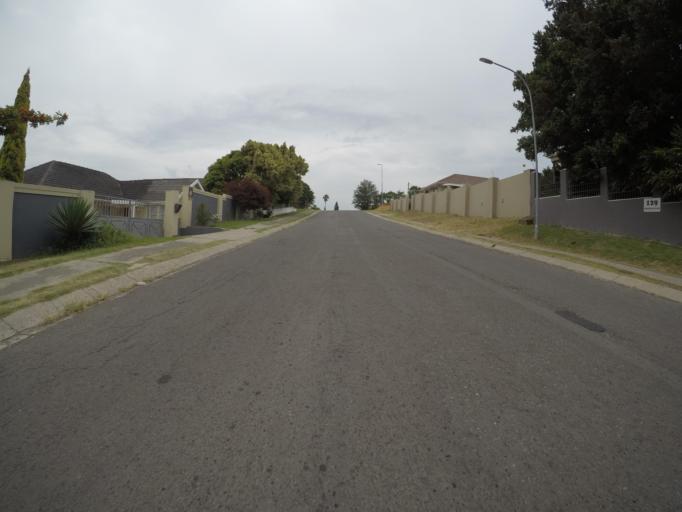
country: ZA
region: Eastern Cape
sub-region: Buffalo City Metropolitan Municipality
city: East London
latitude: -32.9956
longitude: 27.8600
